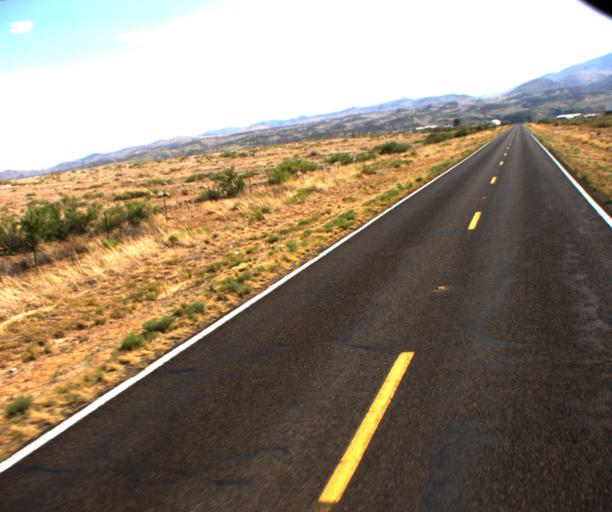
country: US
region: Arizona
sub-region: Greenlee County
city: Clifton
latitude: 32.9553
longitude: -109.2216
